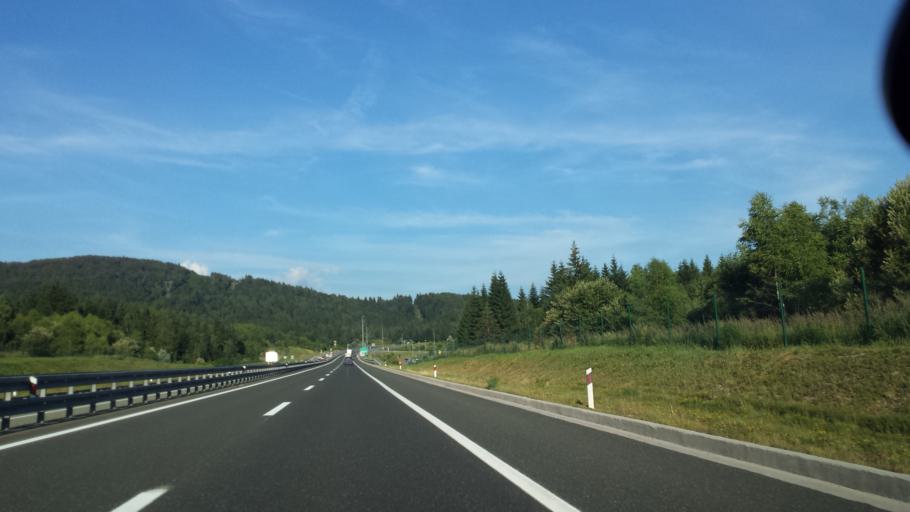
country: SI
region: Kostel
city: Kostel
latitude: 45.3832
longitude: 14.9314
